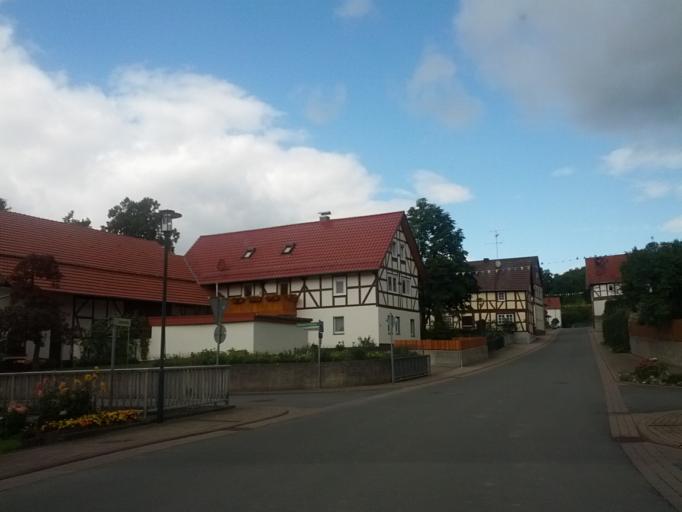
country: DE
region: Hesse
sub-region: Regierungsbezirk Kassel
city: Weissenborn
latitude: 51.0673
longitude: 10.0746
